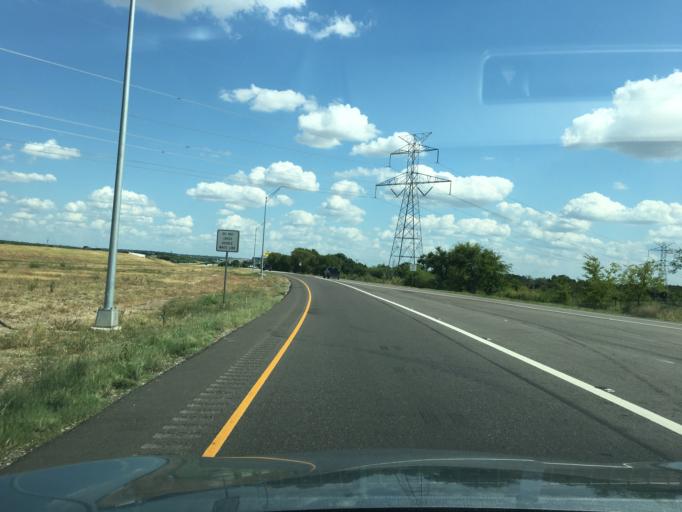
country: US
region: Texas
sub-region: Tarrant County
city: Mansfield
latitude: 32.5186
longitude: -97.0772
